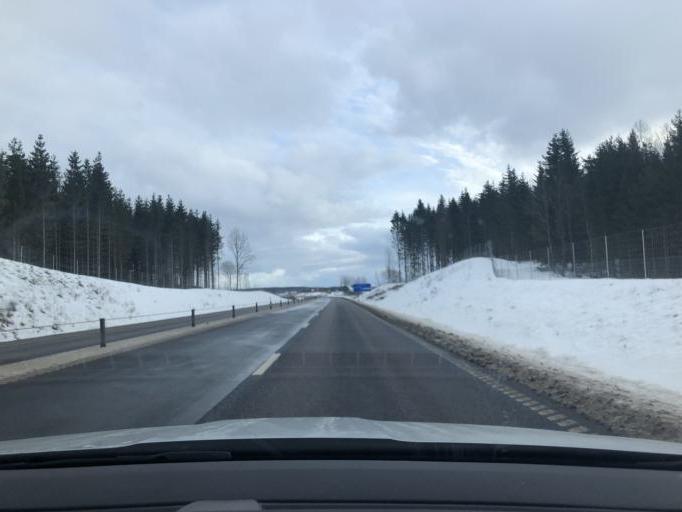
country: SE
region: OEstergoetland
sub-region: Motala Kommun
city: Borensberg
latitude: 58.5866
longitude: 15.1940
